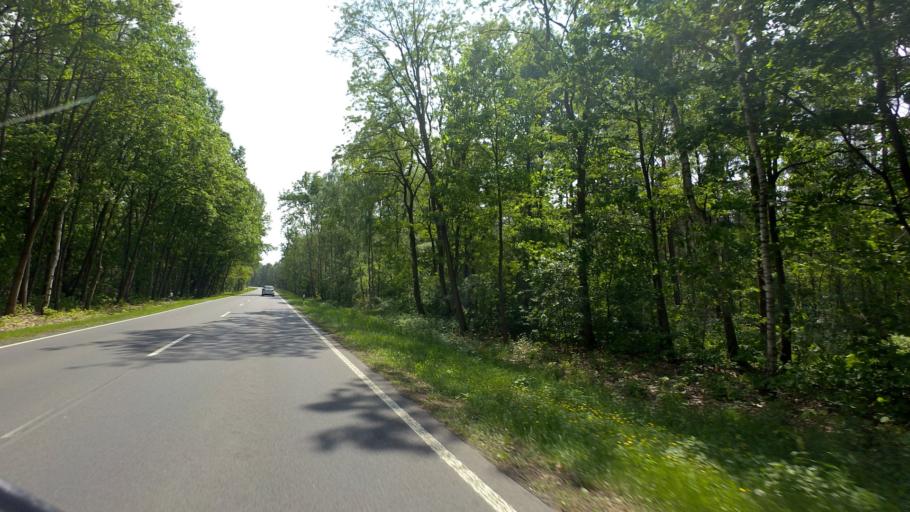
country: DE
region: Saxony
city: Trebendorf
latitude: 51.5316
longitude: 14.5980
